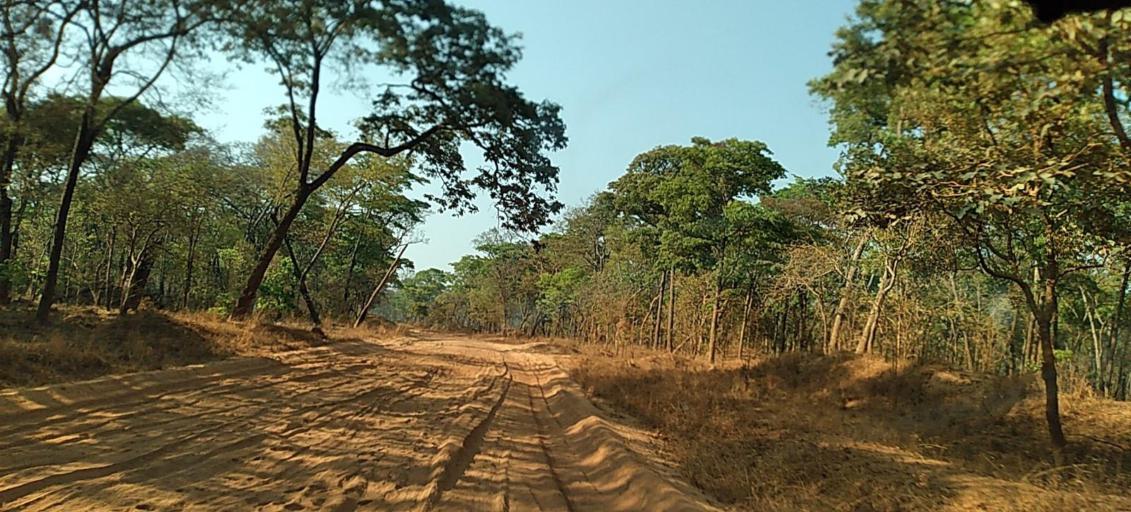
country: ZM
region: North-Western
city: Kasempa
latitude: -13.6158
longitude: 25.9793
